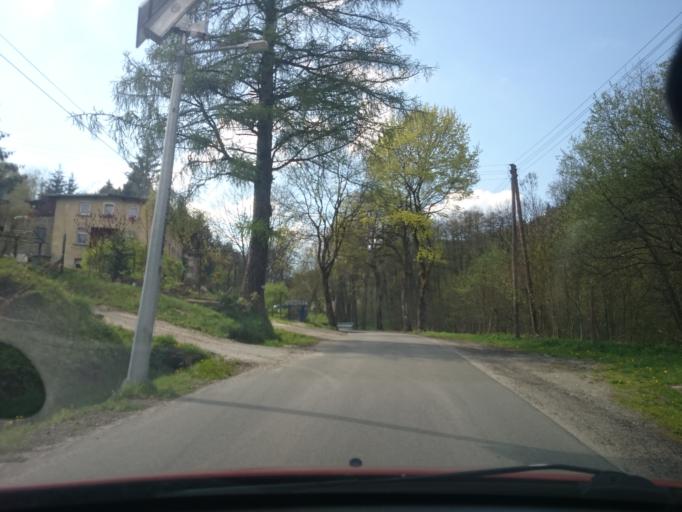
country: PL
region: Lower Silesian Voivodeship
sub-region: Powiat klodzki
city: Bystrzyca Klodzka
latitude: 50.3021
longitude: 16.5379
